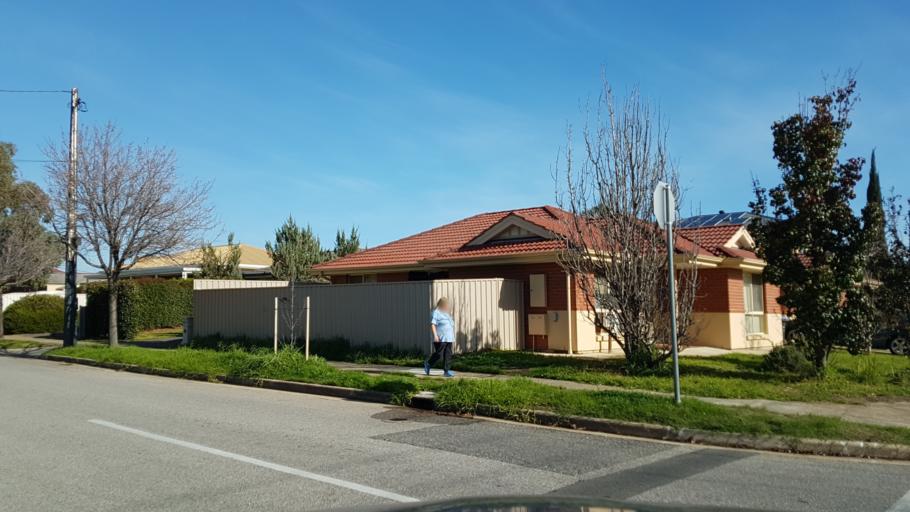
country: AU
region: South Australia
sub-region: Charles Sturt
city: Seaton
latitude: -34.8977
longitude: 138.5176
